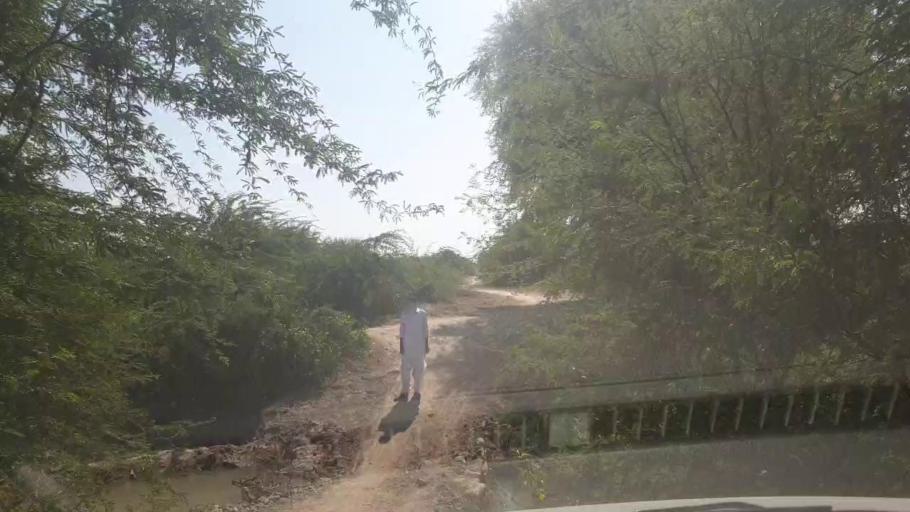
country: PK
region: Sindh
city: Tando Bago
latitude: 24.8986
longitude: 69.1645
